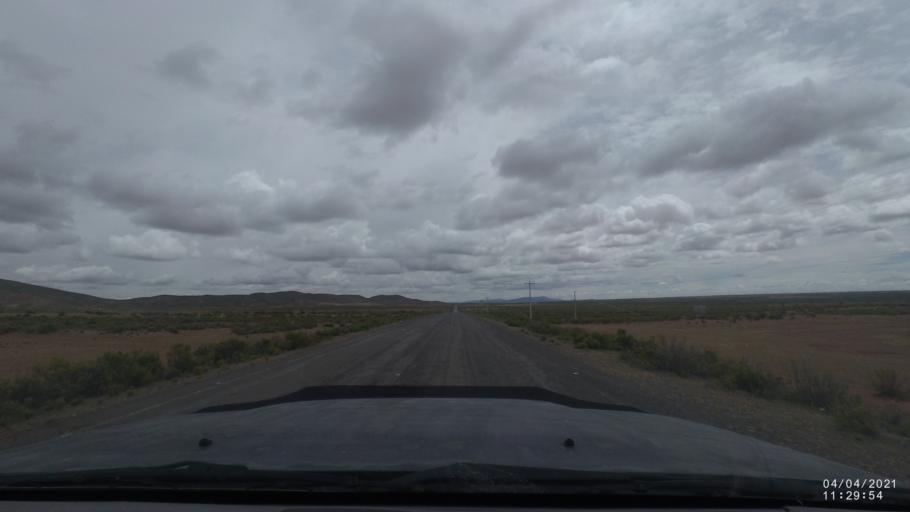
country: BO
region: Oruro
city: Poopo
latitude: -18.6030
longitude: -67.5798
